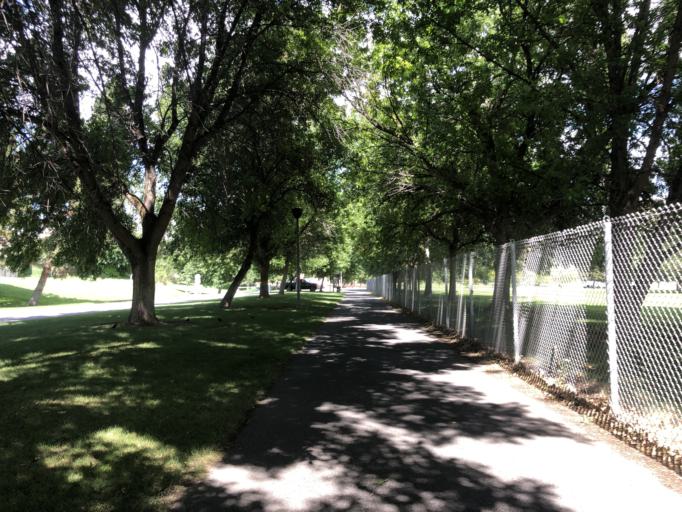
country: US
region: Washington
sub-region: Chelan County
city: Sunnyslope
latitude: 47.4595
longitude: -120.3311
